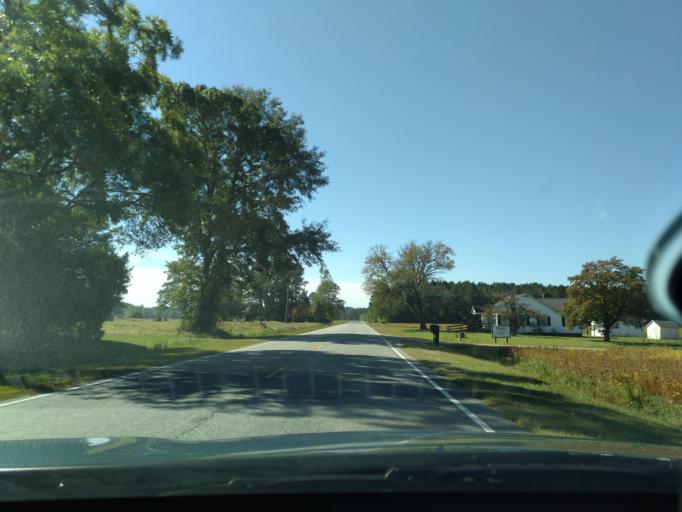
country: US
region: North Carolina
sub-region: Washington County
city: Plymouth
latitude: 35.6853
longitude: -76.7774
